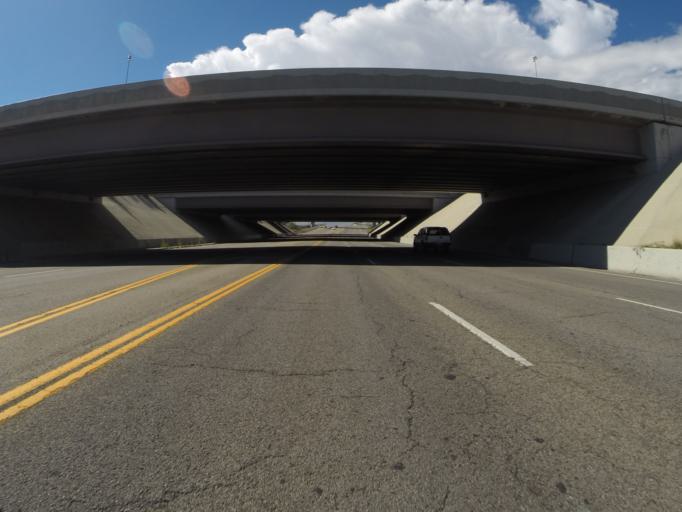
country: US
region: Utah
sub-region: Salt Lake County
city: South Salt Lake
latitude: 40.7254
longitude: -111.9034
